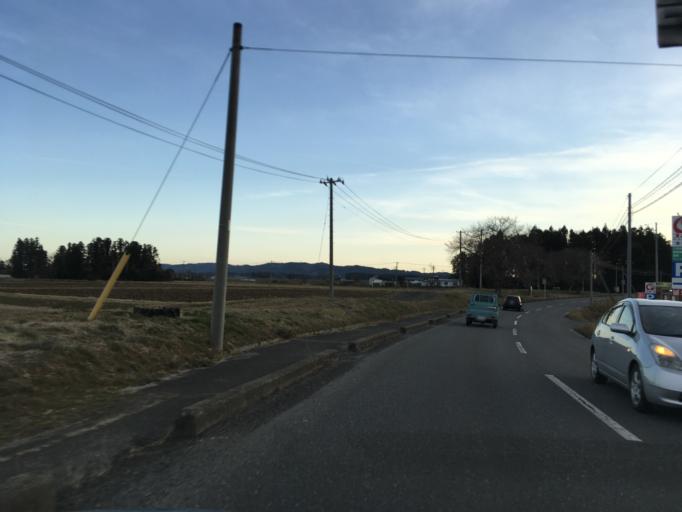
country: JP
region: Miyagi
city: Kogota
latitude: 38.6496
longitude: 141.0758
